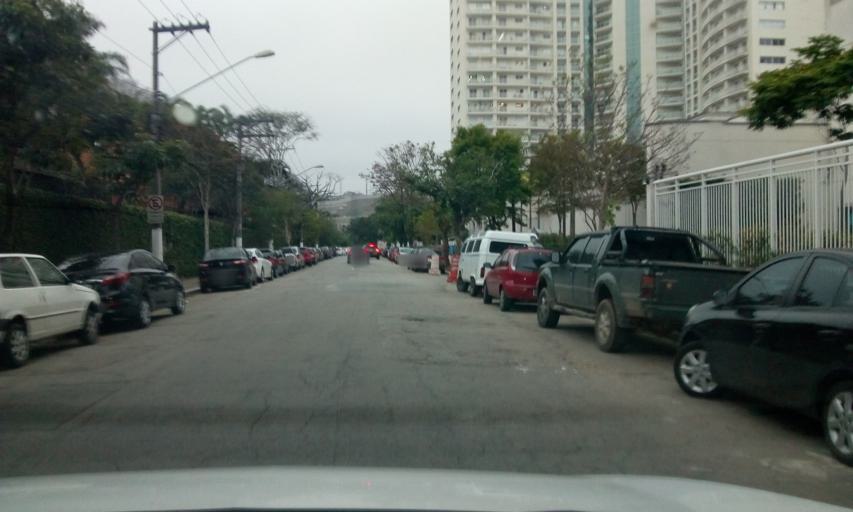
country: BR
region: Sao Paulo
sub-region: Taboao Da Serra
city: Taboao da Serra
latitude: -23.6530
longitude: -46.7189
